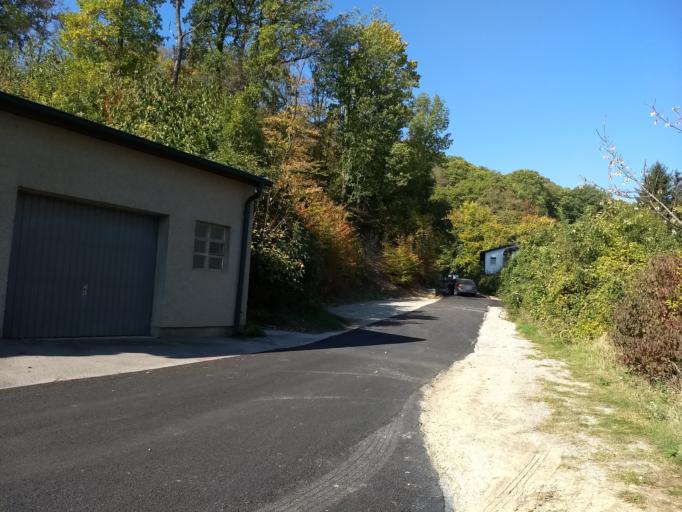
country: AT
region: Lower Austria
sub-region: Politischer Bezirk Modling
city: Giesshubl
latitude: 48.1045
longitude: 16.2396
